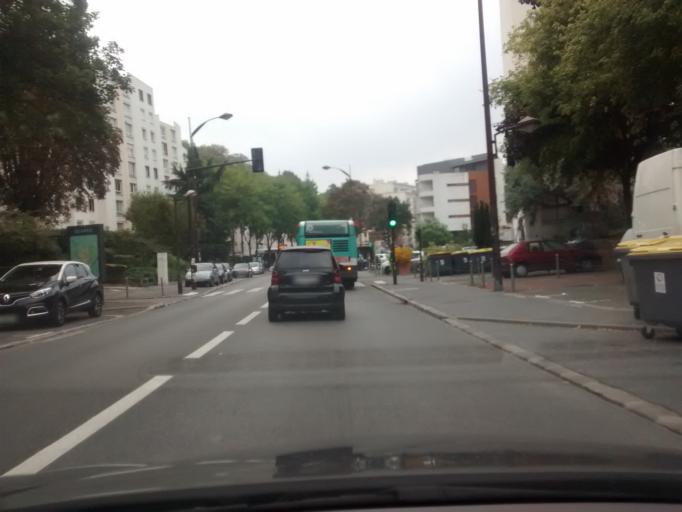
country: FR
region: Ile-de-France
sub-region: Departement des Hauts-de-Seine
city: Ville-d'Avray
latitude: 48.8203
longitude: 2.2008
